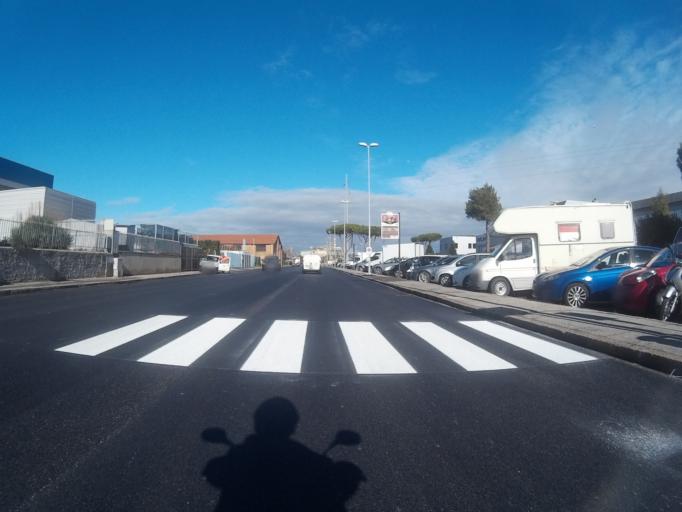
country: IT
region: Tuscany
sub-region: Provincia di Livorno
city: Livorno
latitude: 43.5629
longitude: 10.3420
